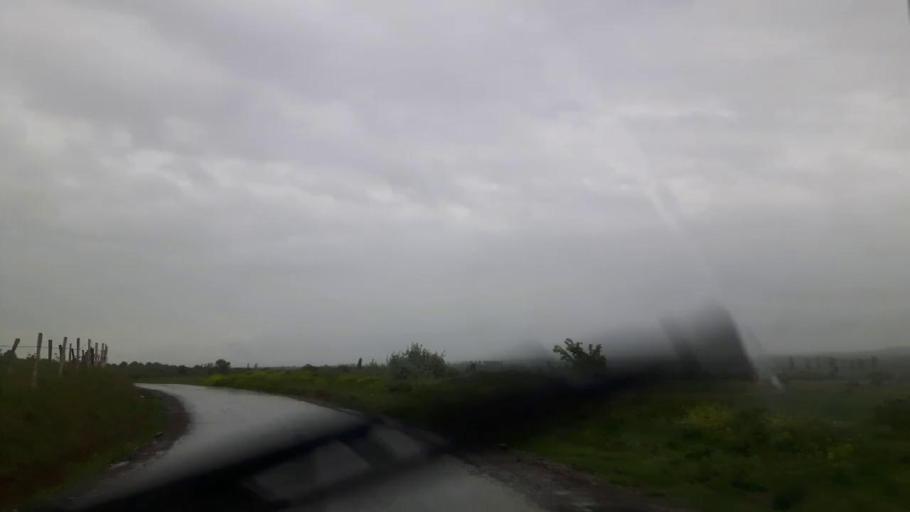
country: GE
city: Agara
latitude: 41.9823
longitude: 43.9512
